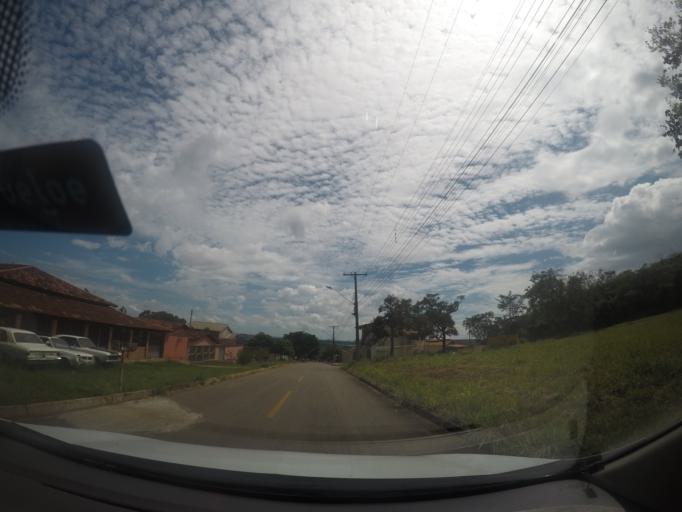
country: BR
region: Goias
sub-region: Goiania
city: Goiania
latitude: -16.6639
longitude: -49.3473
